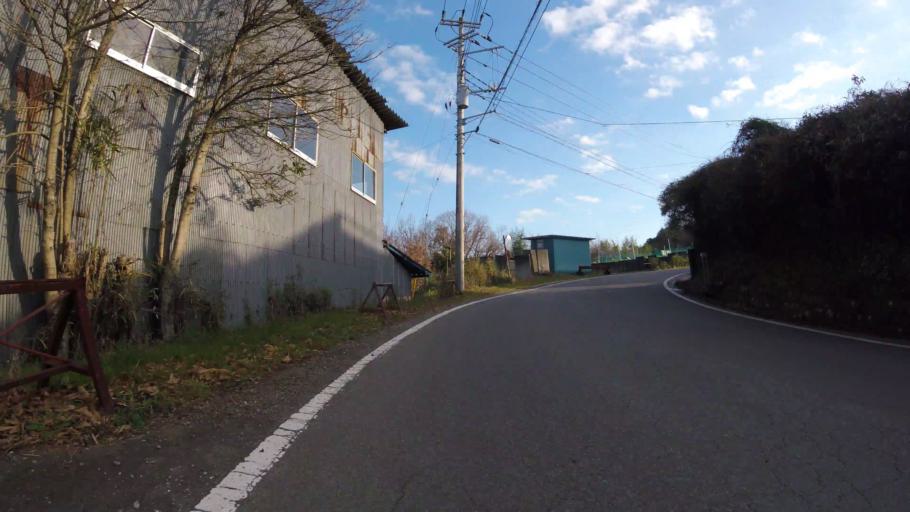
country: JP
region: Shizuoka
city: Mishima
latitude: 35.1066
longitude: 138.9755
